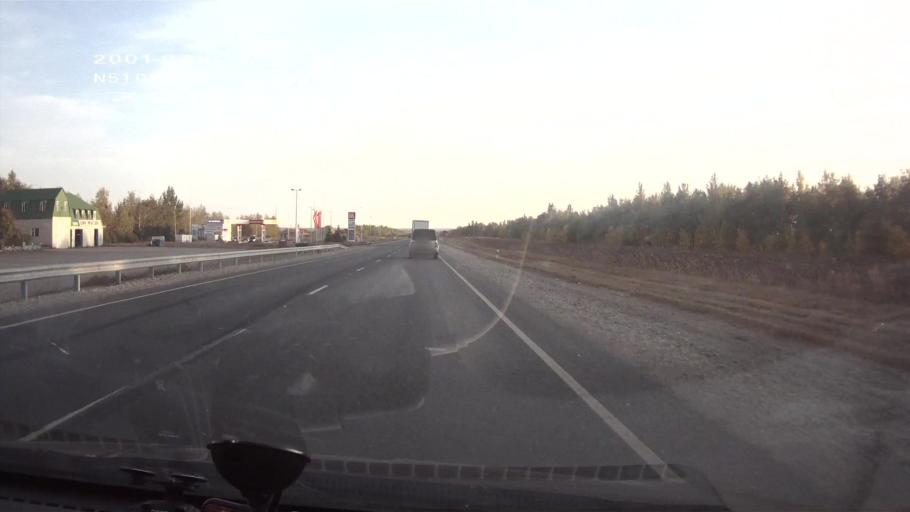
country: RU
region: Saratov
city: Krasnoarmeysk
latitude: 51.0284
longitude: 45.6242
